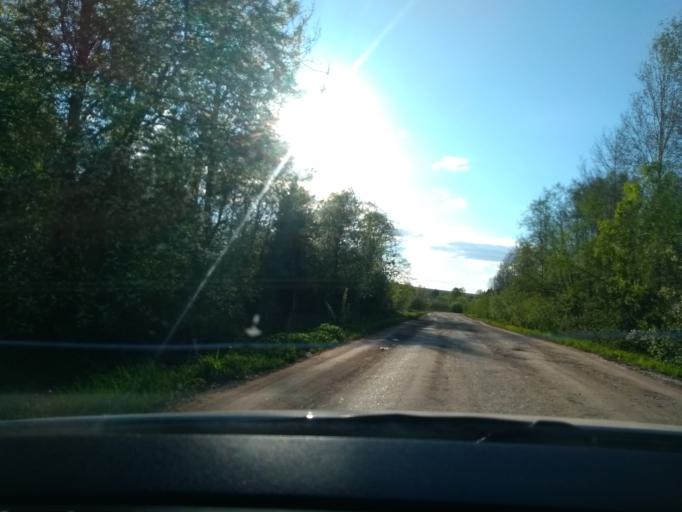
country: RU
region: Perm
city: Sylva
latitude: 57.8340
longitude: 56.6827
